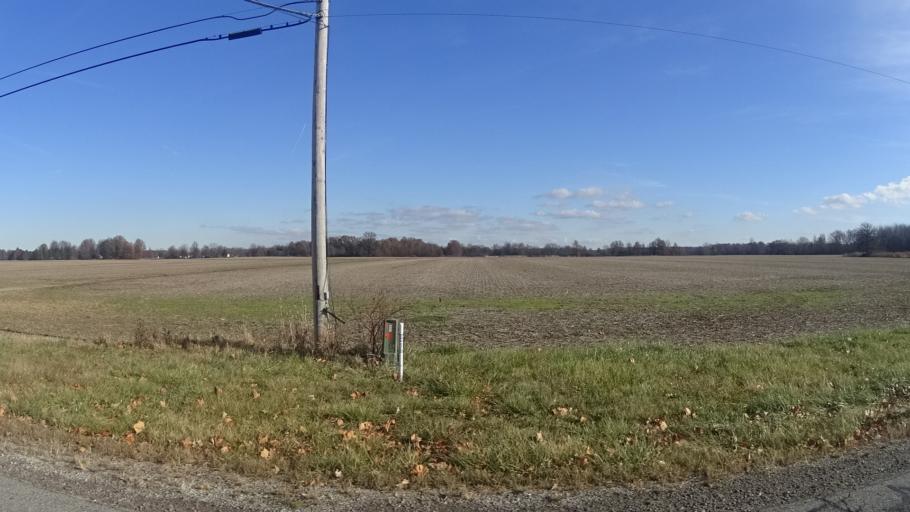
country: US
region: Ohio
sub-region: Lorain County
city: Eaton Estates
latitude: 41.3358
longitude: -81.9906
